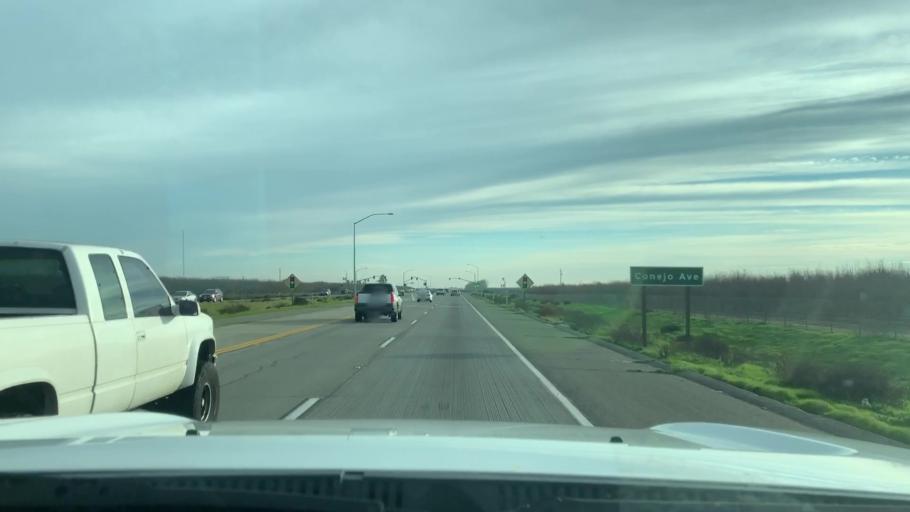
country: US
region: California
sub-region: Fresno County
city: Caruthers
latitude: 36.5213
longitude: -119.7864
